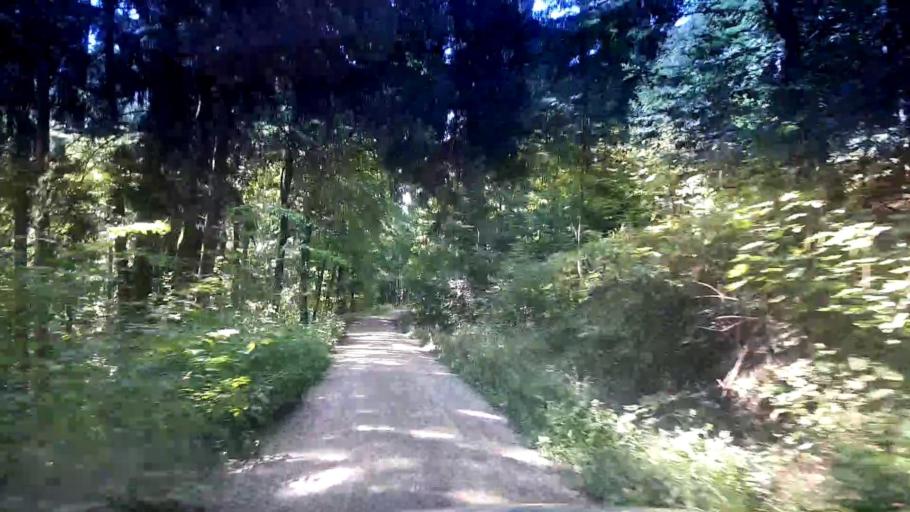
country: DE
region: Bavaria
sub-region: Upper Franconia
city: Litzendorf
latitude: 49.8827
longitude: 11.0361
